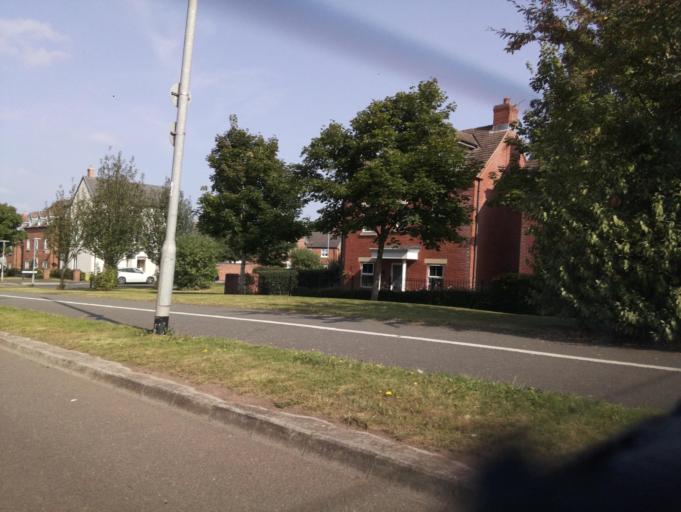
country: GB
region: England
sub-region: Staffordshire
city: Lichfield
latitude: 52.6709
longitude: -1.8392
